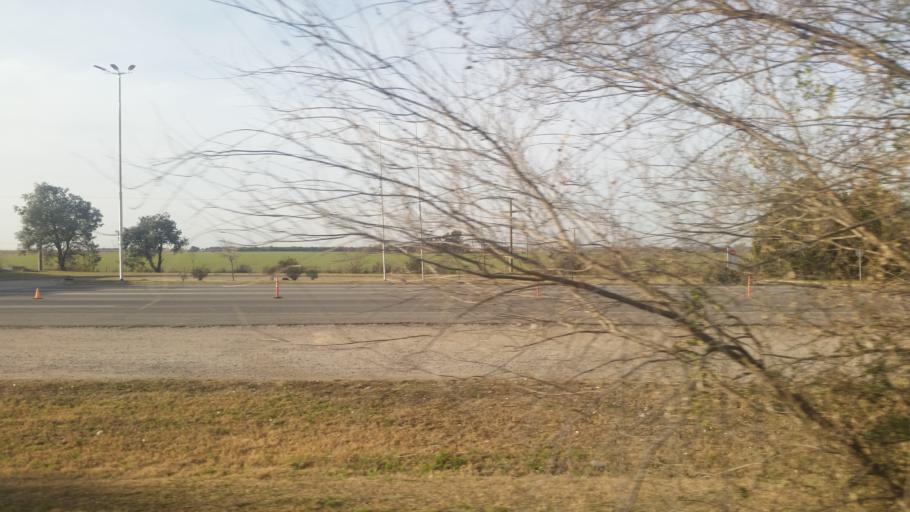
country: AR
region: Cordoba
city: Toledo
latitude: -31.5699
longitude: -63.9953
